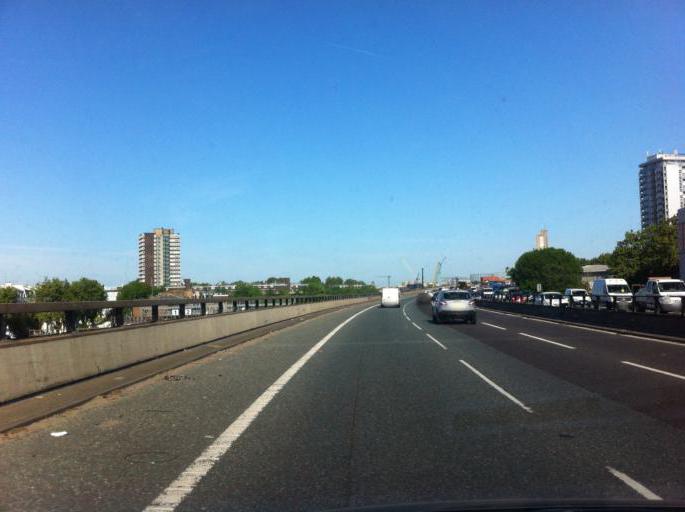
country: GB
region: England
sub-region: Greater London
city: Bayswater
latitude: 51.5196
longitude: -0.1911
